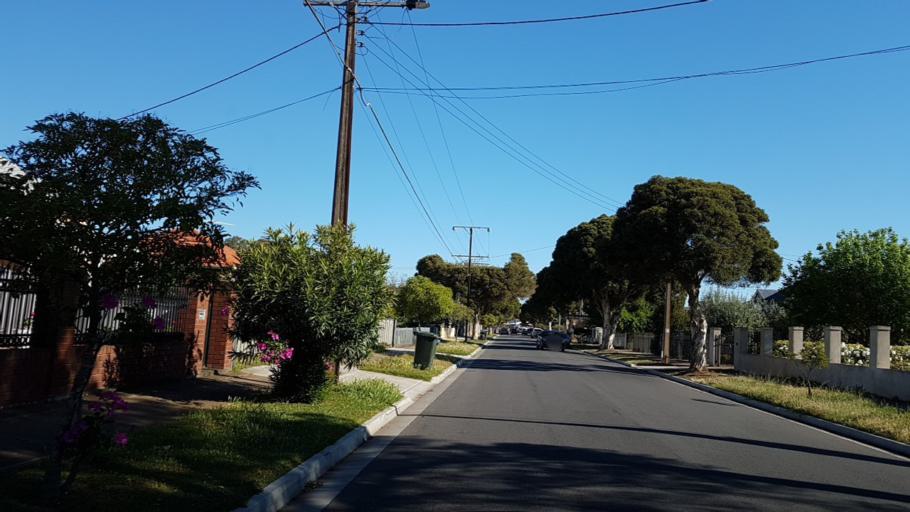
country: AU
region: South Australia
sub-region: Charles Sturt
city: Woodville North
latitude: -34.8692
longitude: 138.5422
